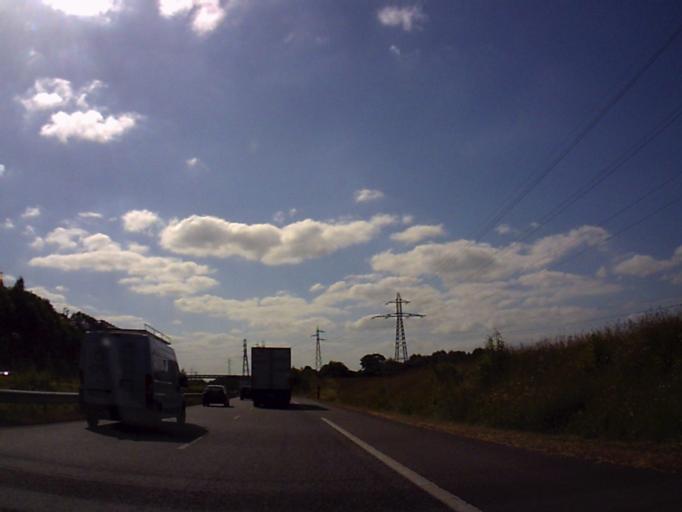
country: FR
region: Brittany
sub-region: Departement d'Ille-et-Vilaine
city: Betton
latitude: 48.1419
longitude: -1.6440
